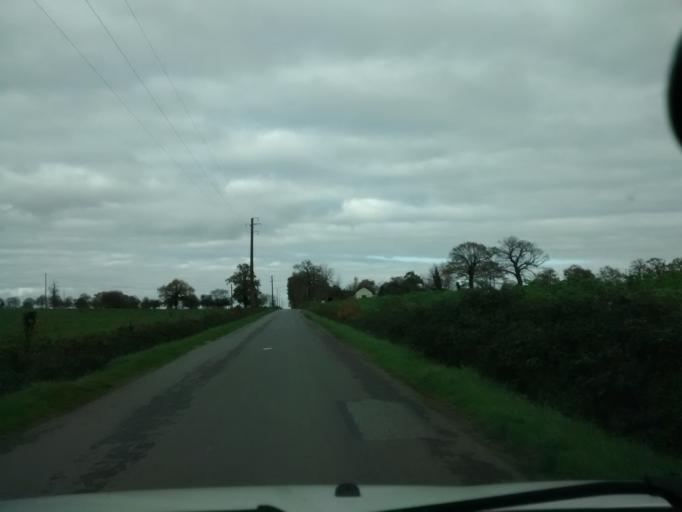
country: FR
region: Brittany
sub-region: Departement d'Ille-et-Vilaine
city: Argentre-du-Plessis
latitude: 48.0824
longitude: -1.1546
